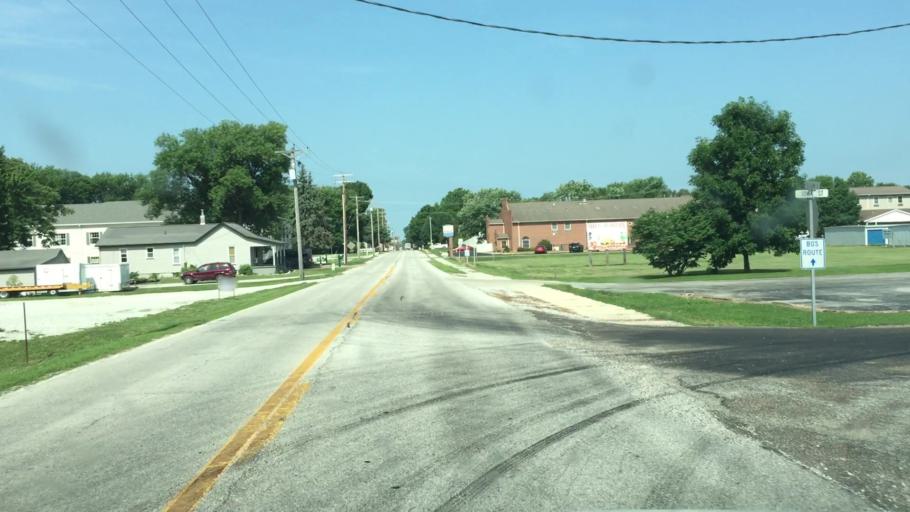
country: US
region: Illinois
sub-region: Hancock County
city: Nauvoo
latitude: 40.5496
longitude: -91.3705
